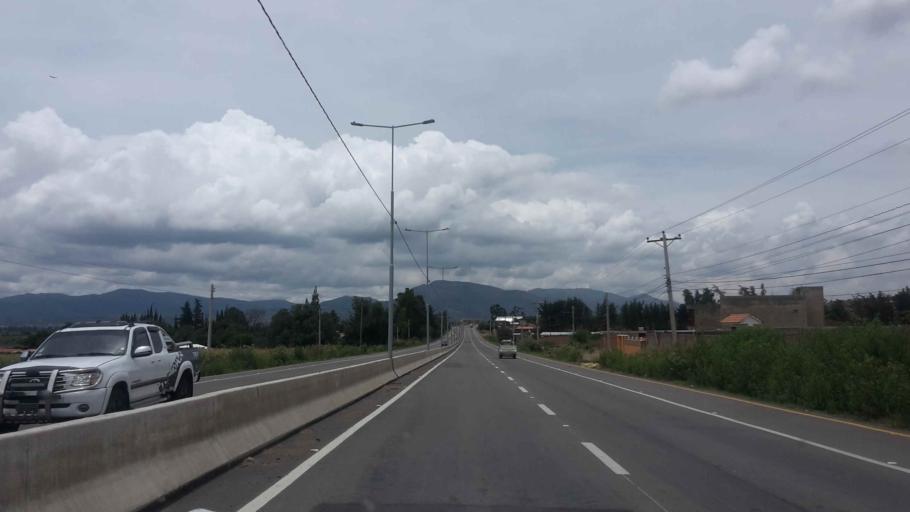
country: BO
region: Cochabamba
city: Cliza
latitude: -17.5357
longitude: -65.9827
